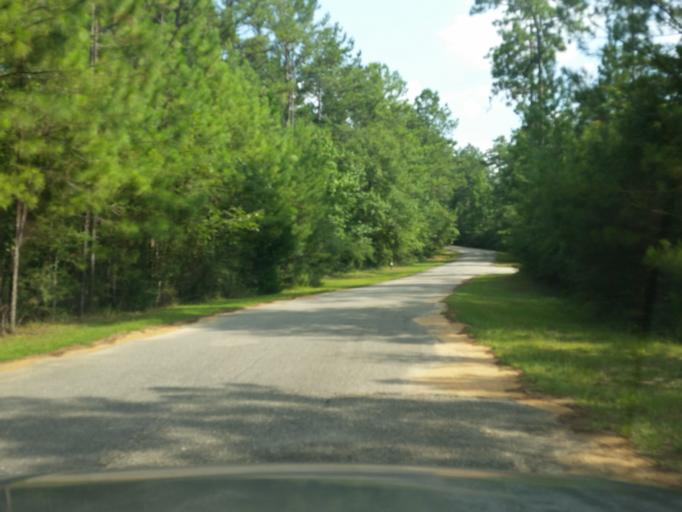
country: US
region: Alabama
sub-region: Baldwin County
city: Spanish Fort
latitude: 30.7365
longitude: -87.9059
